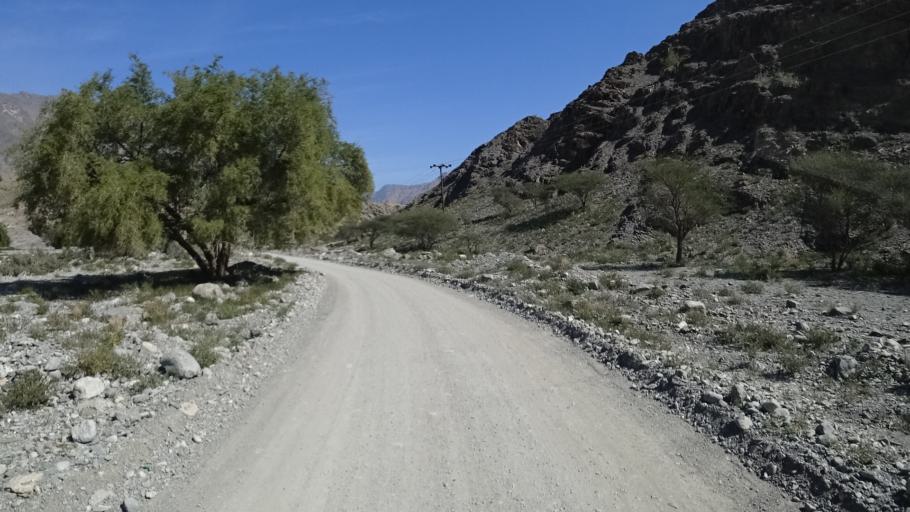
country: OM
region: Al Batinah
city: Bayt al `Awabi
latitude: 23.2574
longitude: 57.4305
